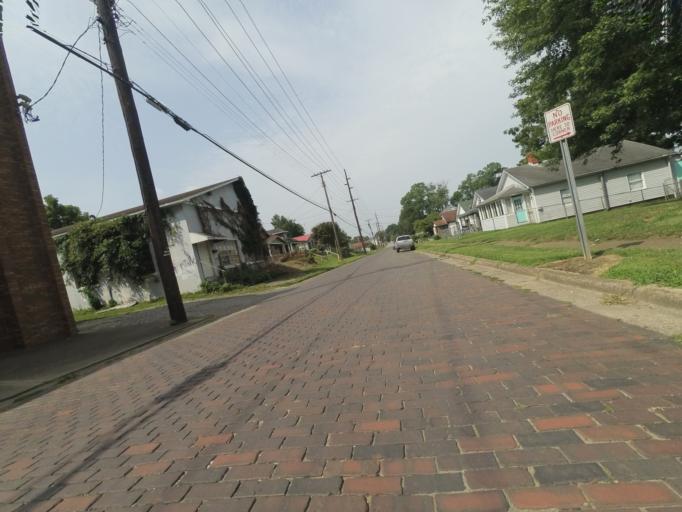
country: US
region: West Virginia
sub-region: Cabell County
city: Huntington
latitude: 38.4107
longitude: -82.4652
